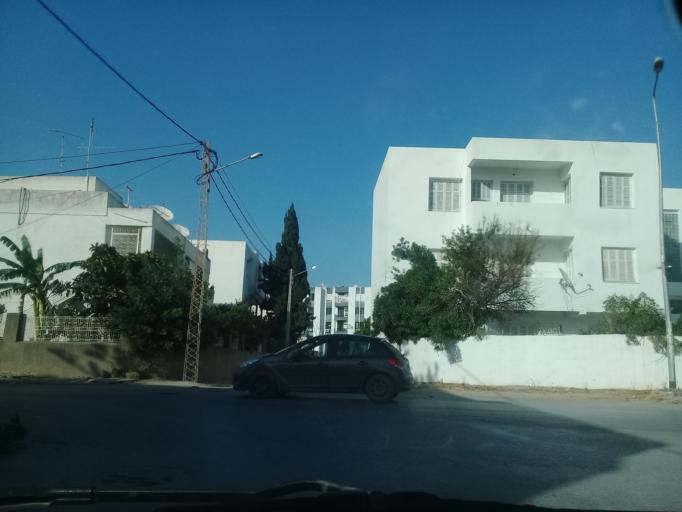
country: TN
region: Ariana
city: Ariana
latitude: 36.8358
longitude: 10.1975
